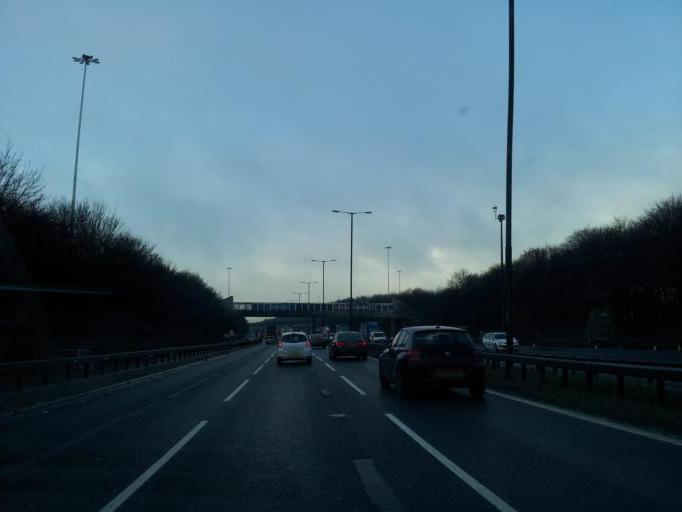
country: GB
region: England
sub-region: Manchester
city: Heywood
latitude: 53.5685
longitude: -2.2296
